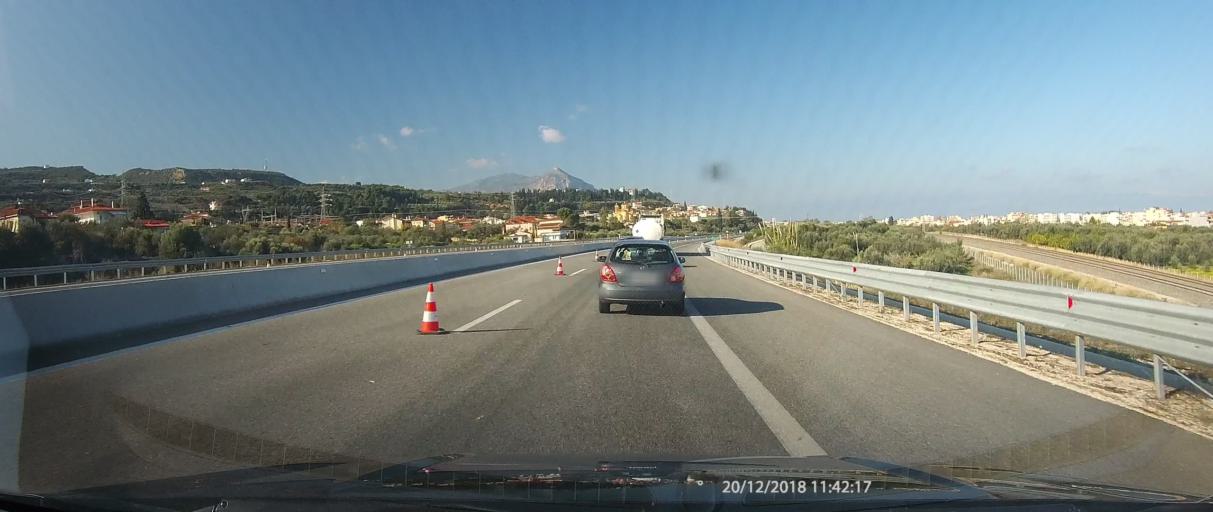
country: GR
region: Peloponnese
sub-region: Nomos Korinthias
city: Xylokastro
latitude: 38.0656
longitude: 22.6480
